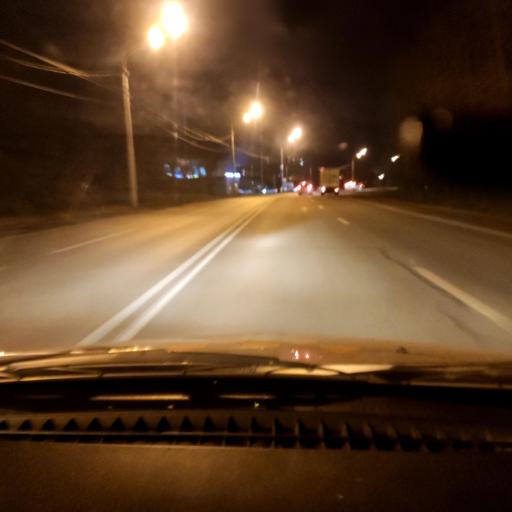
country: RU
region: Bashkortostan
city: Avdon
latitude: 54.6903
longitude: 55.8178
